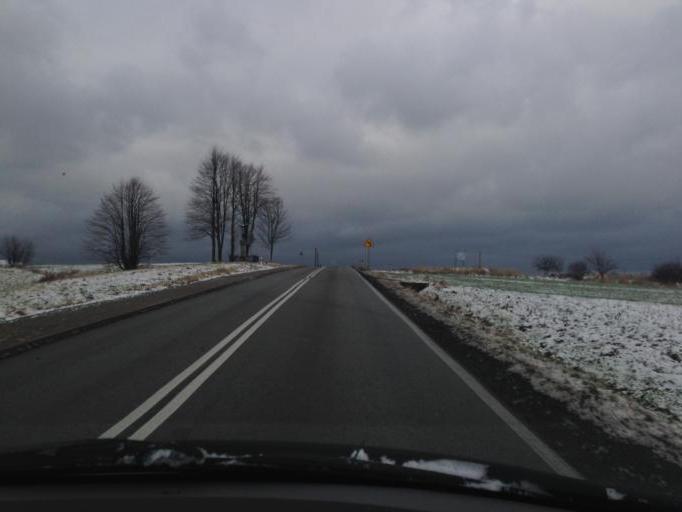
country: PL
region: Lesser Poland Voivodeship
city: Stary Wisnicz
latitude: 49.8540
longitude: 20.5174
